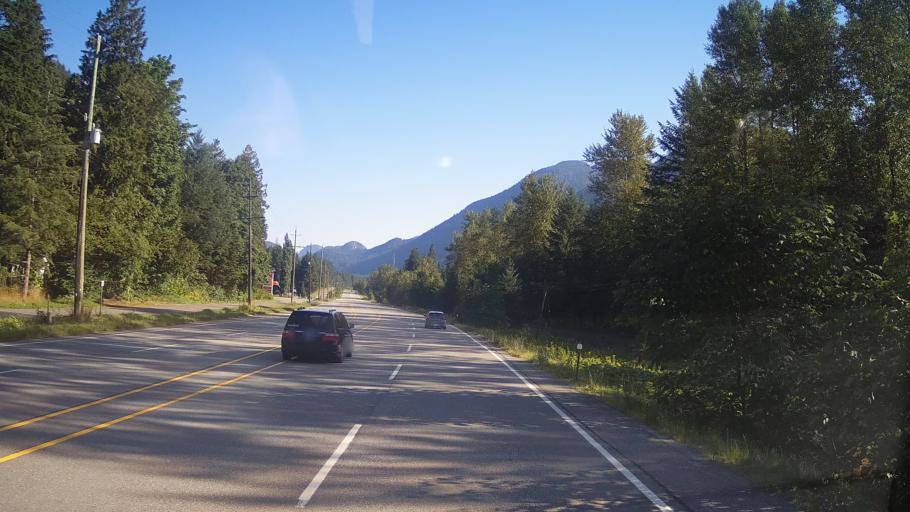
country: CA
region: British Columbia
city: Hope
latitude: 49.4856
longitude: -121.4214
